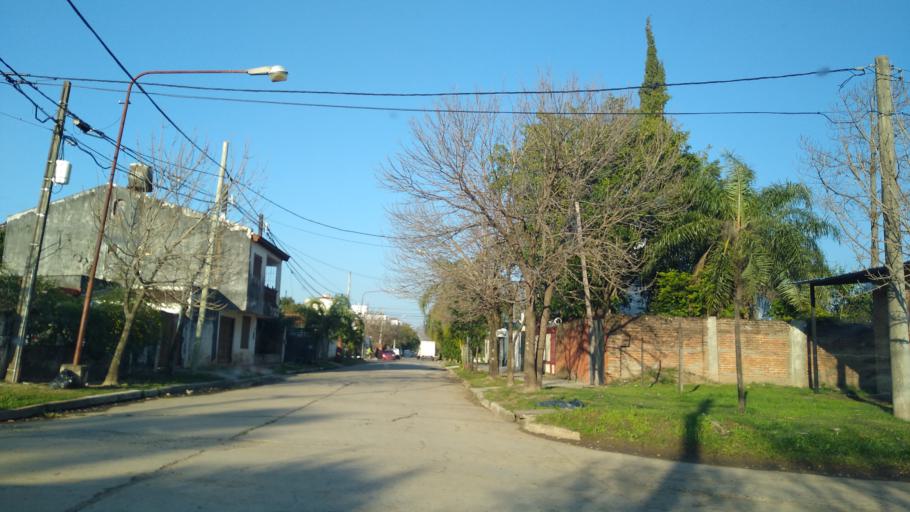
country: AR
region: Chaco
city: Barranqueras
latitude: -27.4795
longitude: -58.9487
